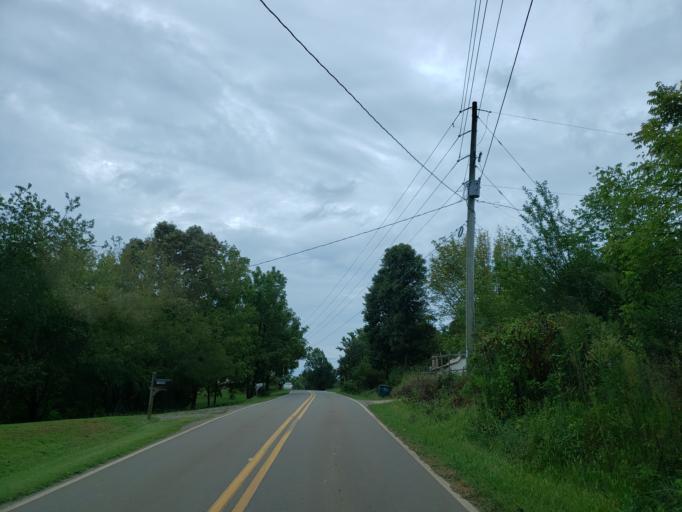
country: US
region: Georgia
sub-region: Pickens County
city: Jasper
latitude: 34.4261
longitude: -84.5520
